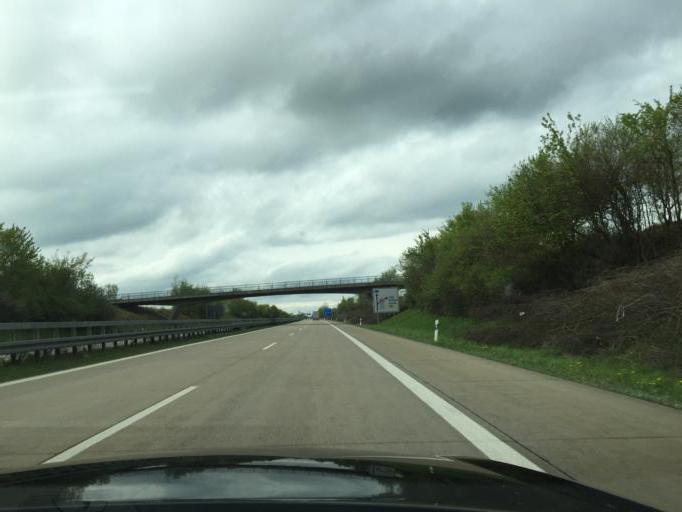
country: DE
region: Baden-Wuerttemberg
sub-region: Regierungsbezirk Stuttgart
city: Ellwangen
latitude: 48.9456
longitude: 10.1910
